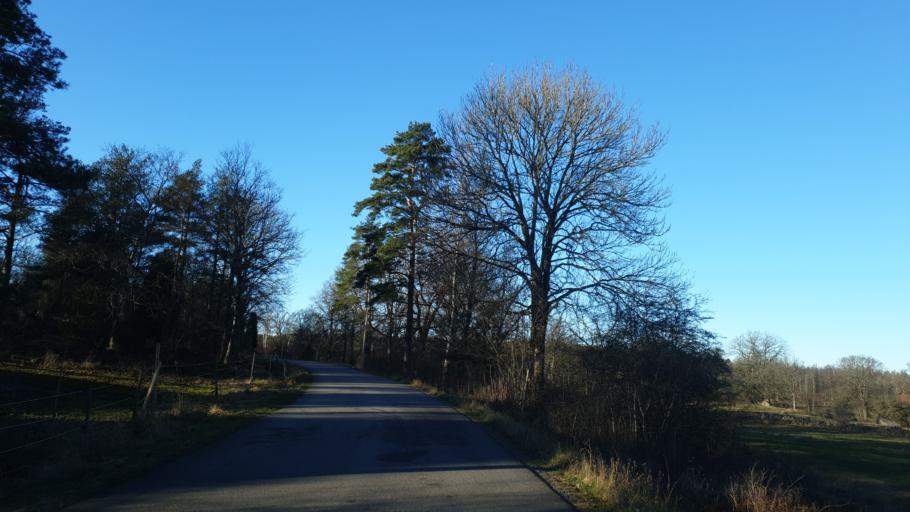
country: SE
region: Blekinge
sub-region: Karlskrona Kommun
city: Nattraby
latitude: 56.2704
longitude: 15.4608
